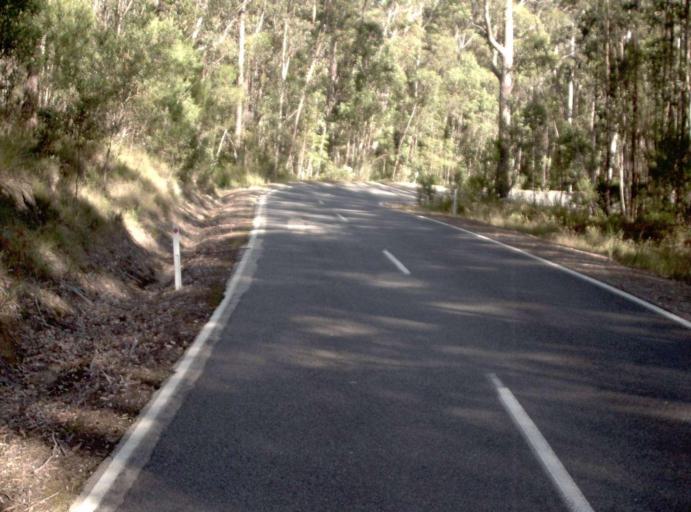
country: AU
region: Victoria
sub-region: East Gippsland
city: Lakes Entrance
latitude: -37.6268
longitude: 148.5058
